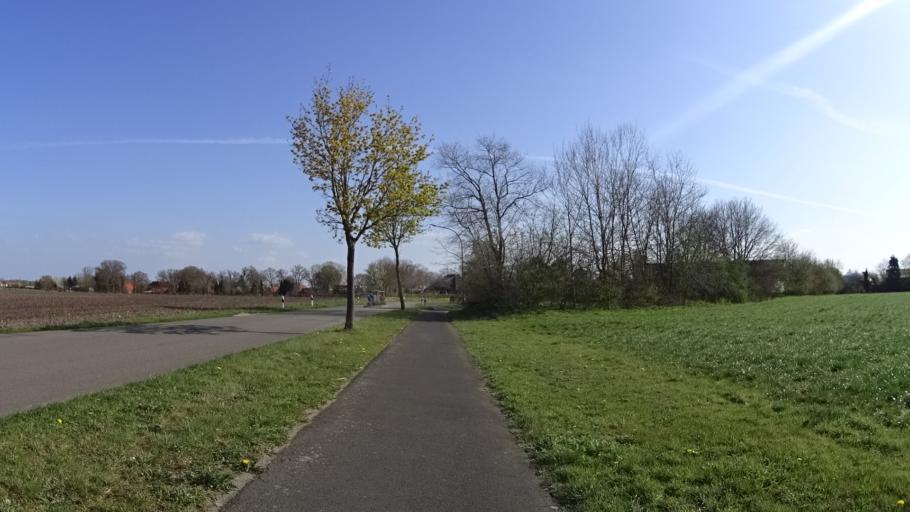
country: DE
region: Lower Saxony
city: Dorpen
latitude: 52.9416
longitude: 7.3176
